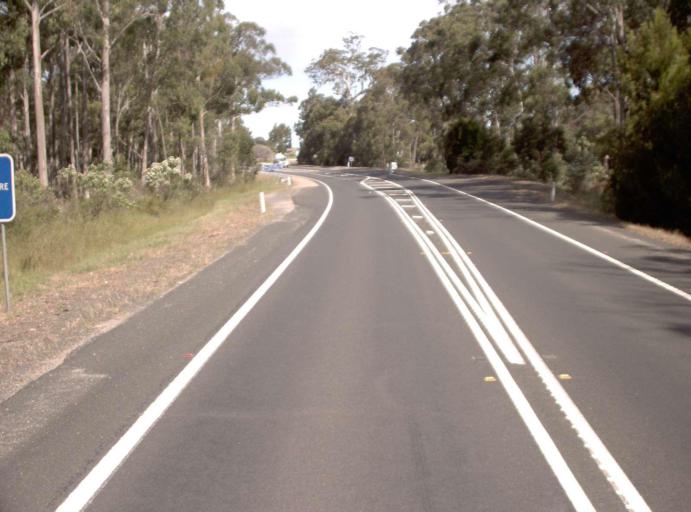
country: AU
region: Victoria
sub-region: East Gippsland
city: Lakes Entrance
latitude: -37.8377
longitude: 147.9207
